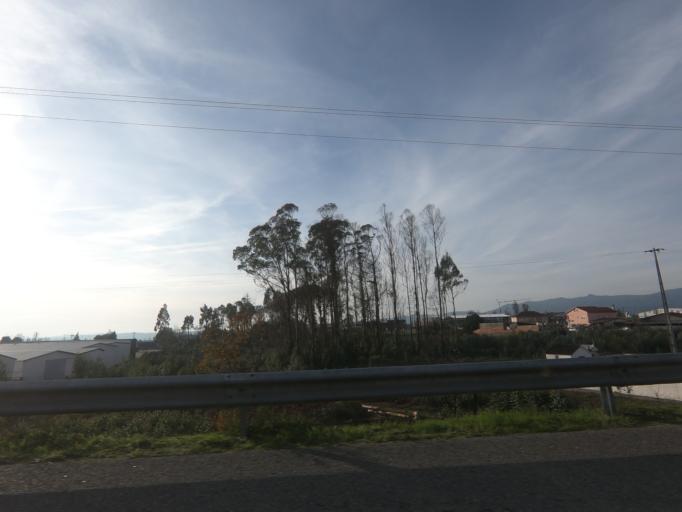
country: PT
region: Viseu
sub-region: Concelho de Tondela
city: Tondela
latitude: 40.4865
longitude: -8.0869
